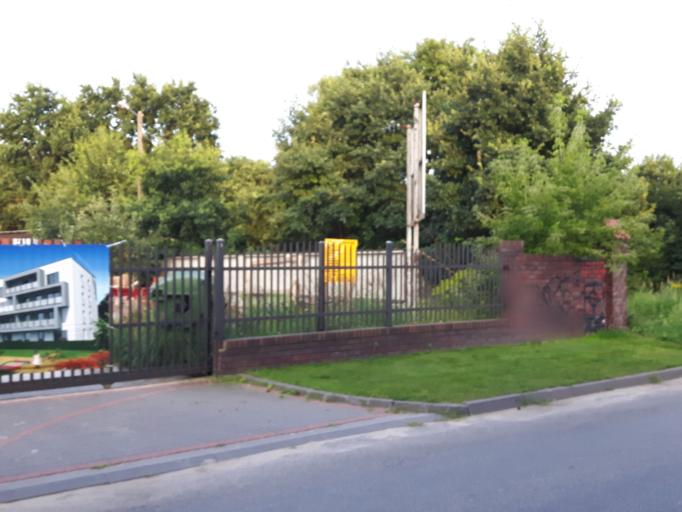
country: PL
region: Masovian Voivodeship
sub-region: Powiat wolominski
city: Zabki
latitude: 52.2858
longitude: 21.1217
